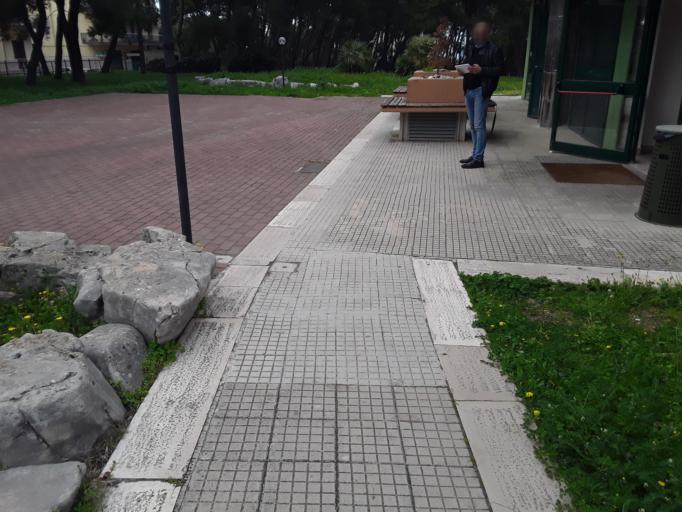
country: IT
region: Apulia
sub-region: Provincia di Bari
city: Ruvo di Puglia
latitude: 41.1215
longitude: 16.4867
